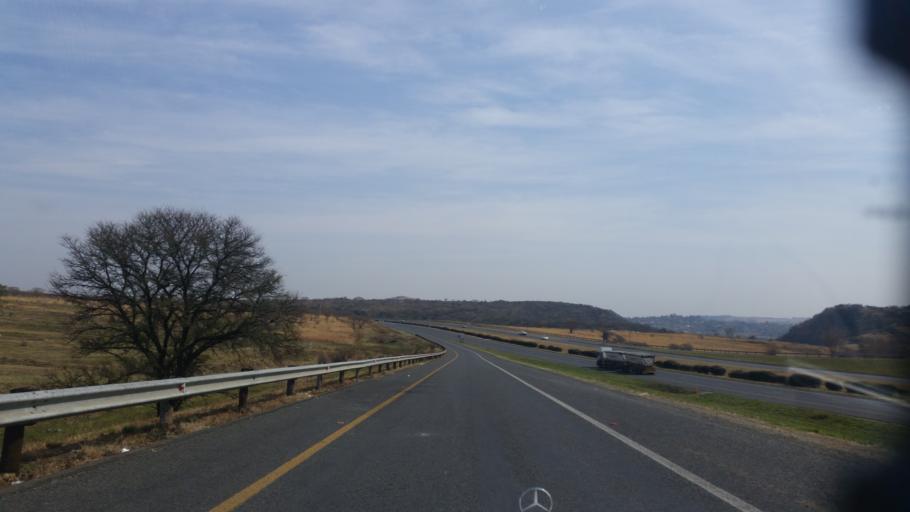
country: ZA
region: KwaZulu-Natal
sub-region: uThukela District Municipality
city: Estcourt
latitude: -29.0487
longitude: 29.8911
